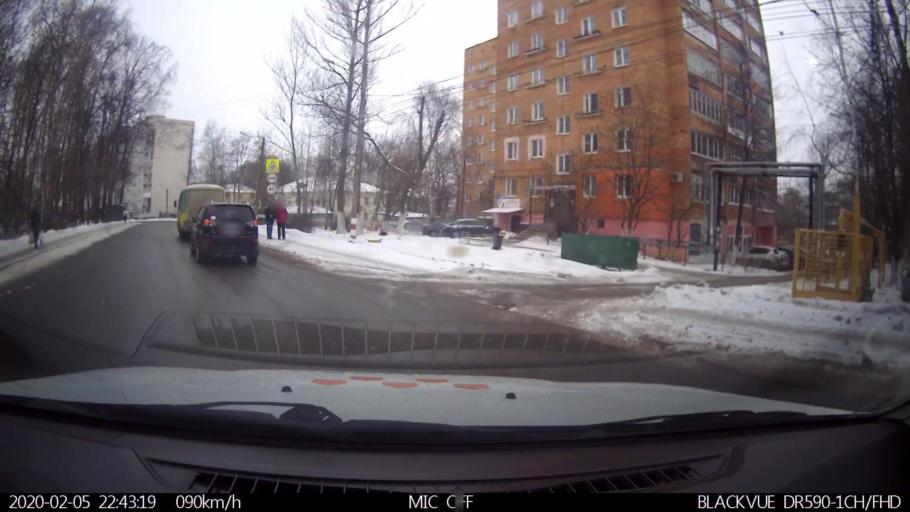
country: RU
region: Nizjnij Novgorod
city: Imeni Stepana Razina
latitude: 54.7135
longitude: 44.3743
